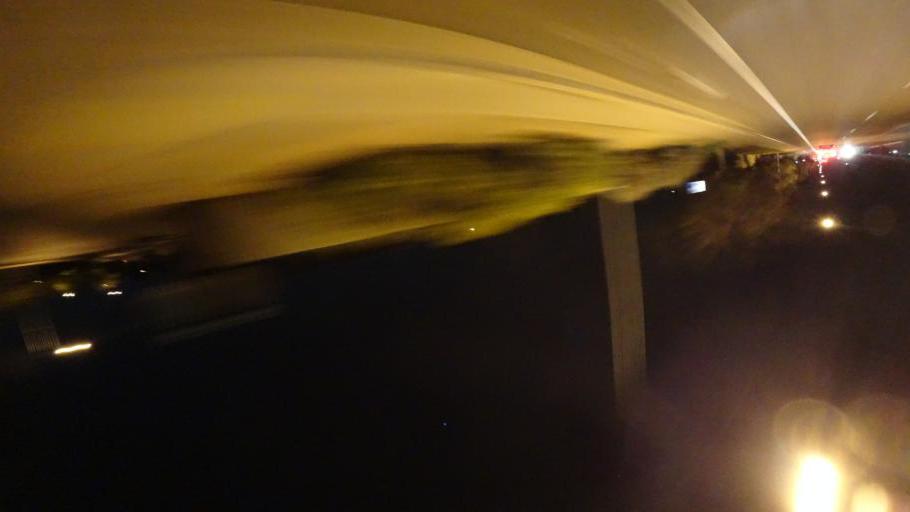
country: US
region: Arizona
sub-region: Maricopa County
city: Mesa
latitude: 33.4373
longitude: -111.7251
